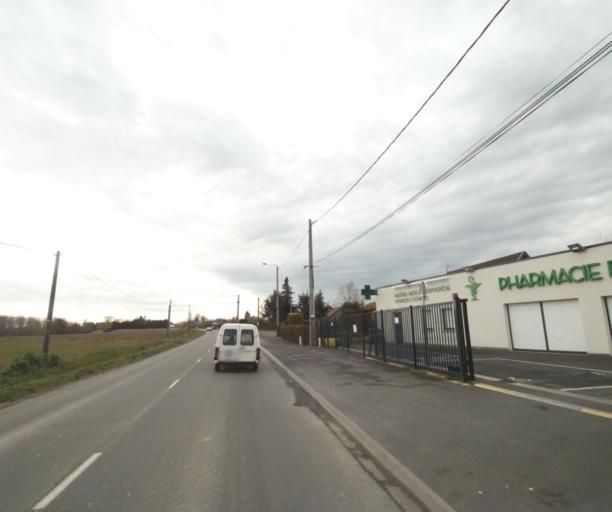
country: FR
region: Nord-Pas-de-Calais
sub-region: Departement du Nord
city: Sebourg
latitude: 50.3495
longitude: 3.6380
